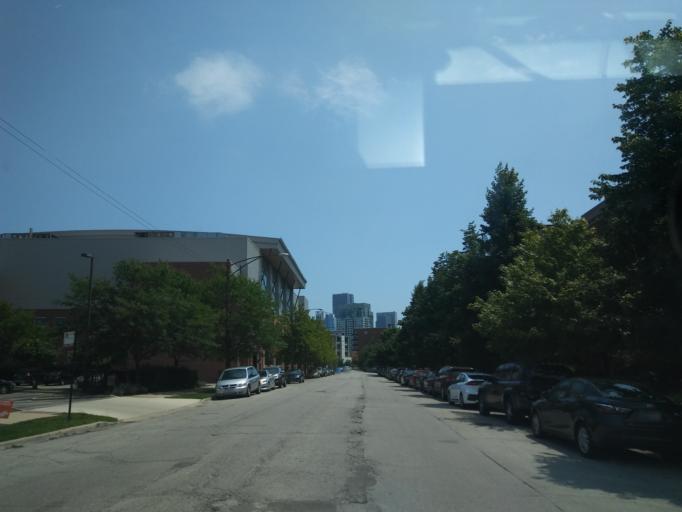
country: US
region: Illinois
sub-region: Cook County
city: Chicago
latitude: 41.9014
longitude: -87.6447
